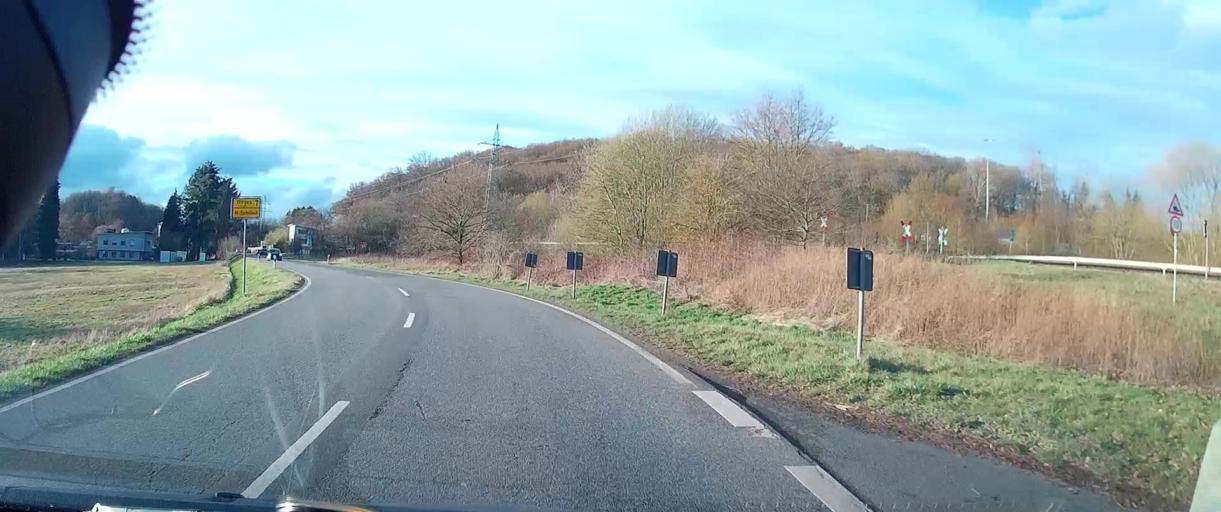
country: DE
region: Rheinland-Pfalz
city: Montabaur
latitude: 50.4493
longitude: 7.8159
